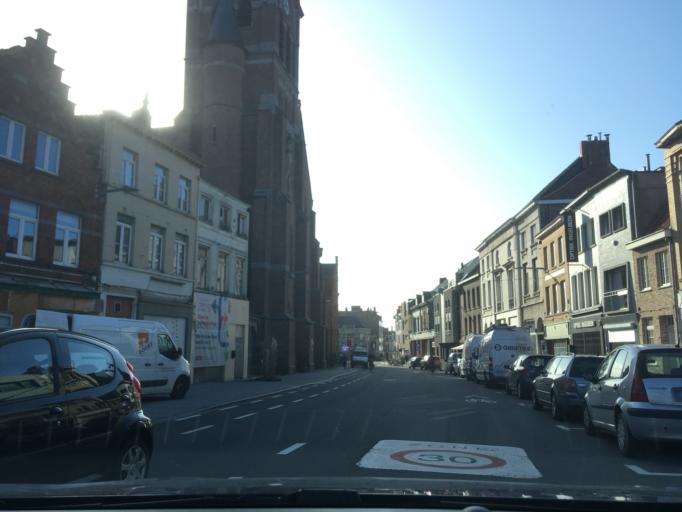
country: BE
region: Flanders
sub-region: Provincie West-Vlaanderen
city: Kortrijk
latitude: 50.8336
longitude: 3.2589
